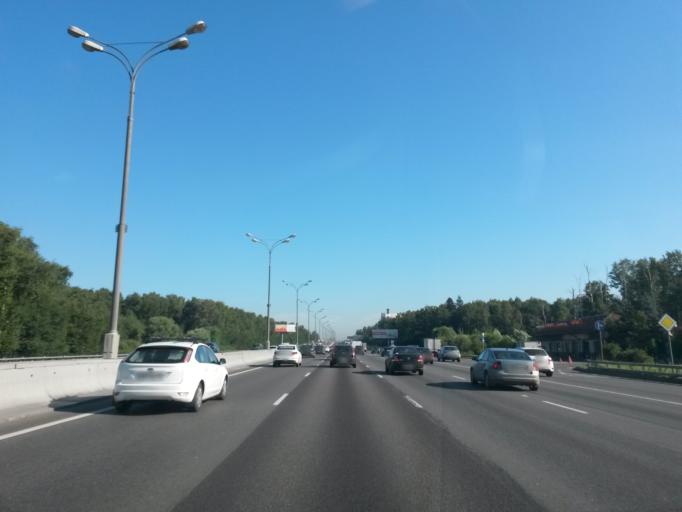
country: RU
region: Moscow
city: Ivanovskoye
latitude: 55.7930
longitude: 37.8411
